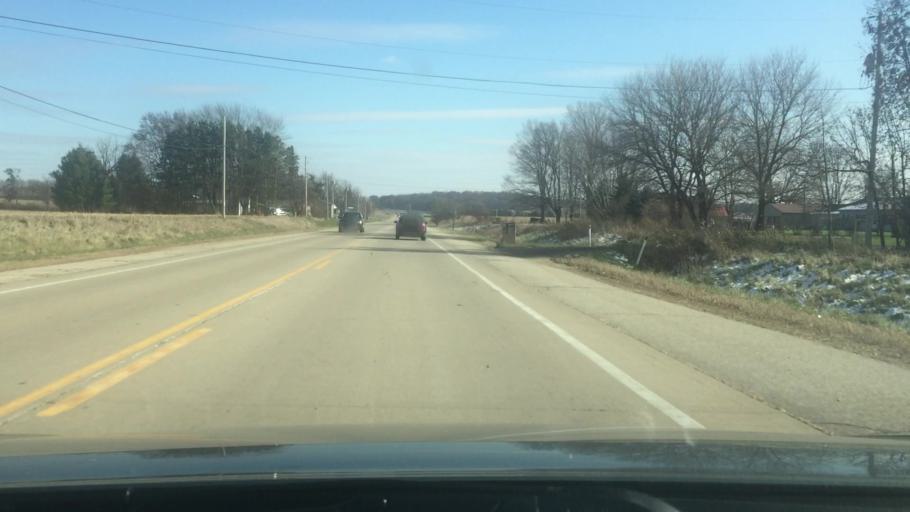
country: US
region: Wisconsin
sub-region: Jefferson County
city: Lake Ripley
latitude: 42.9777
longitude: -88.9587
